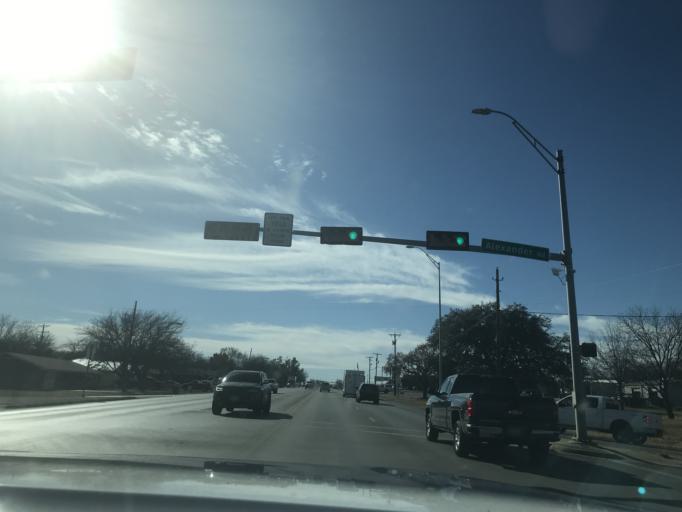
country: US
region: Texas
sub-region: Erath County
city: Stephenville
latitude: 32.2074
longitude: -98.2053
